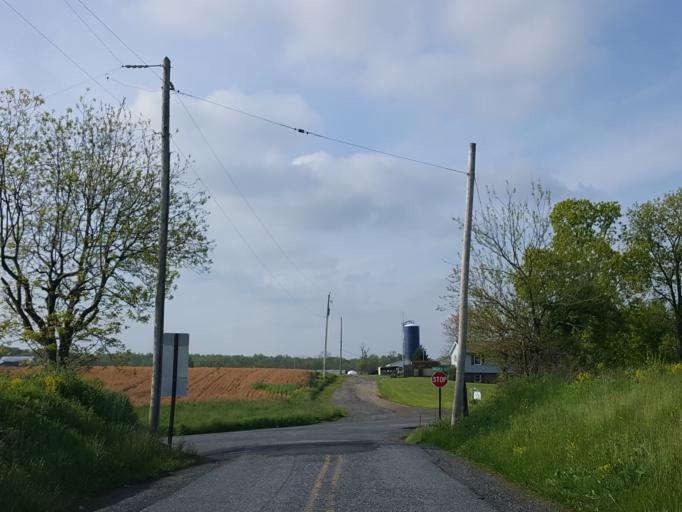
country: US
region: Pennsylvania
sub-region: Lancaster County
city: Elizabethtown
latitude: 40.2030
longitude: -76.5712
